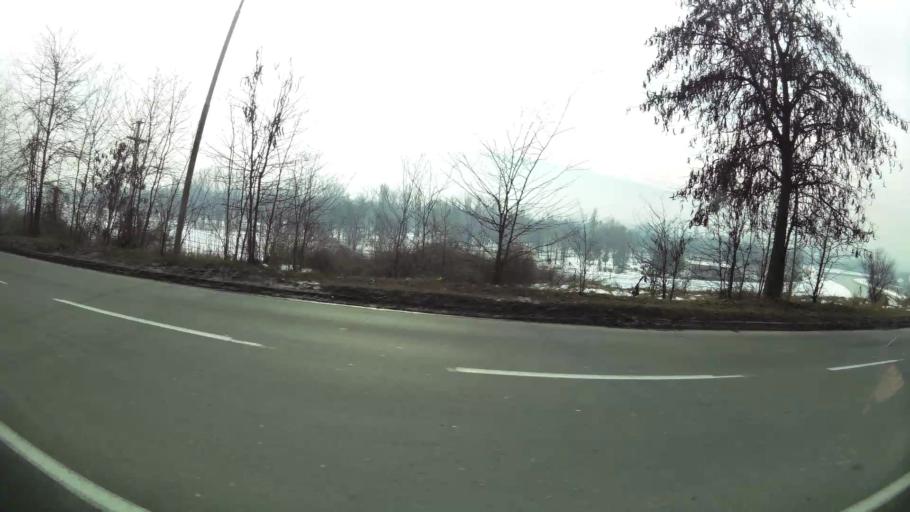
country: MK
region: Karpos
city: Skopje
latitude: 42.0138
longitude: 21.4179
